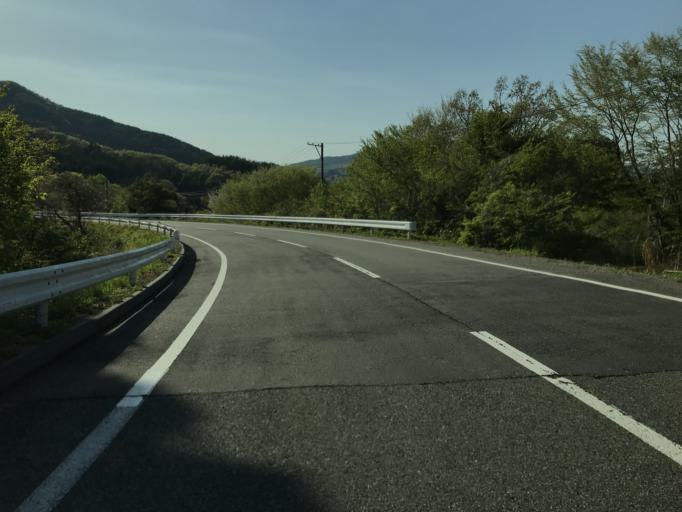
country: JP
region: Fukushima
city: Funehikimachi-funehiki
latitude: 37.5420
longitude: 140.7398
